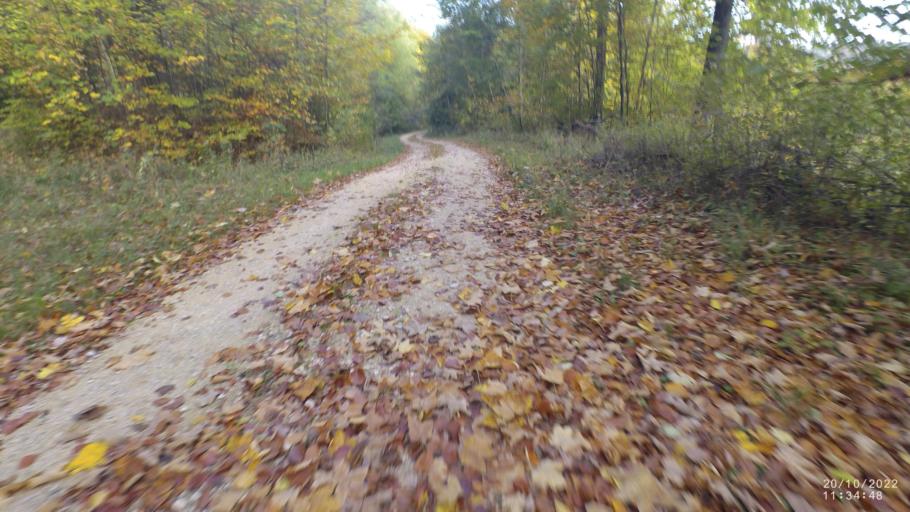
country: DE
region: Baden-Wuerttemberg
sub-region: Regierungsbezirk Stuttgart
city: Aichelberg
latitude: 48.6196
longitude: 9.5843
